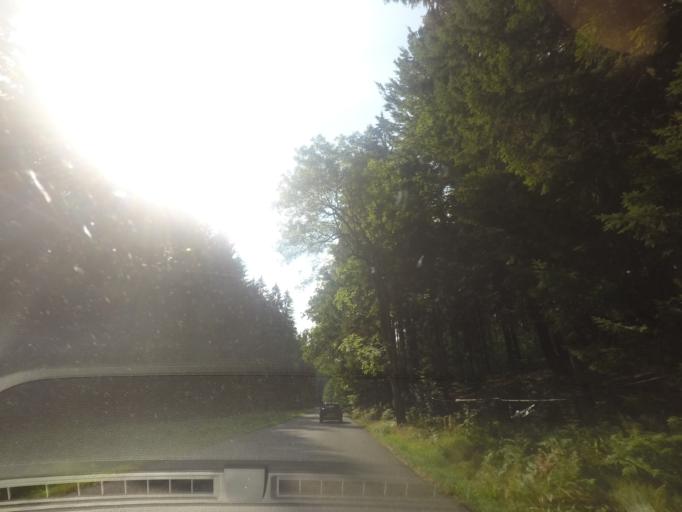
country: DE
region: Saxony
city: Sebnitz
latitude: 50.8753
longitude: 14.2951
